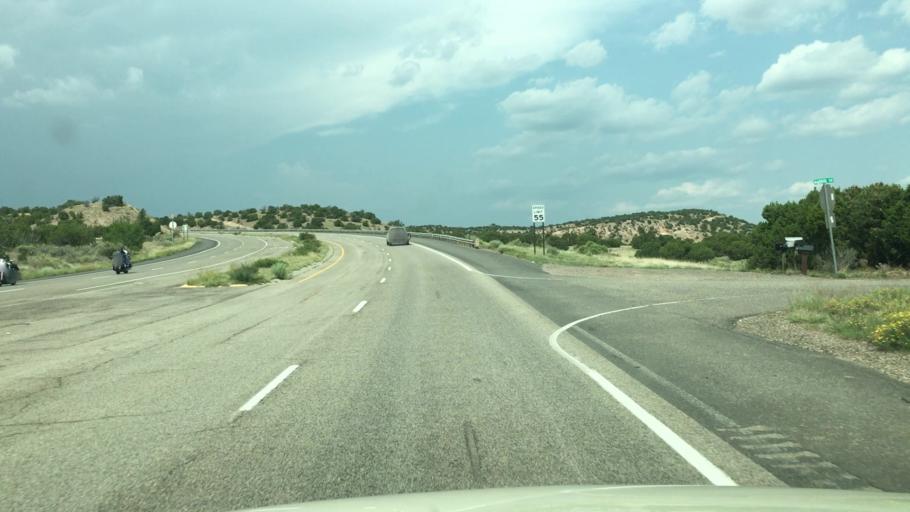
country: US
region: New Mexico
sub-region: Santa Fe County
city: Eldorado at Santa Fe
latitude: 35.4849
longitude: -105.9049
